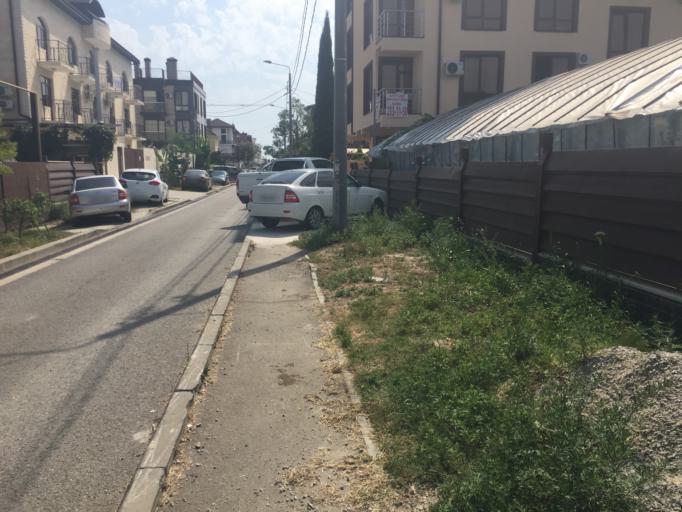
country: RU
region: Krasnodarskiy
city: Adler
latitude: 43.4146
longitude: 39.9622
